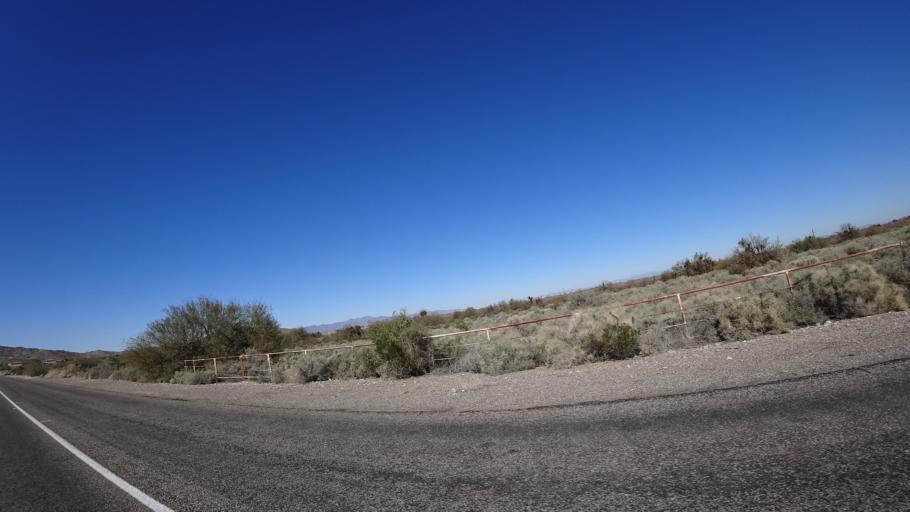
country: US
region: Arizona
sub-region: Maricopa County
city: Avondale
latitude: 33.3756
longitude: -112.3502
